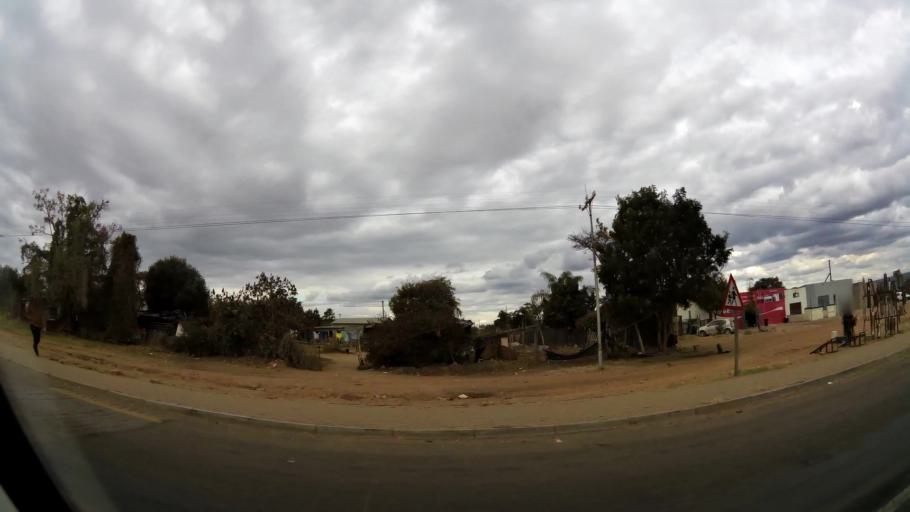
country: ZA
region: Limpopo
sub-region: Waterberg District Municipality
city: Modimolle
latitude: -24.6893
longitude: 28.4193
